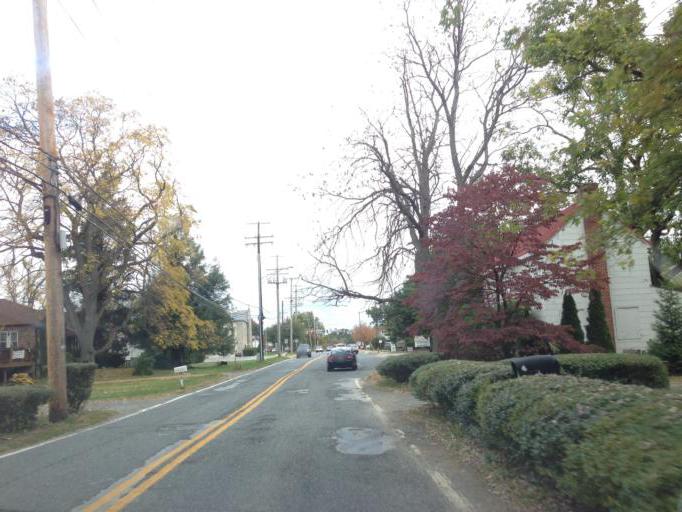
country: US
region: Maryland
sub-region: Baltimore County
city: Milford Mill
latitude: 39.3548
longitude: -76.7667
